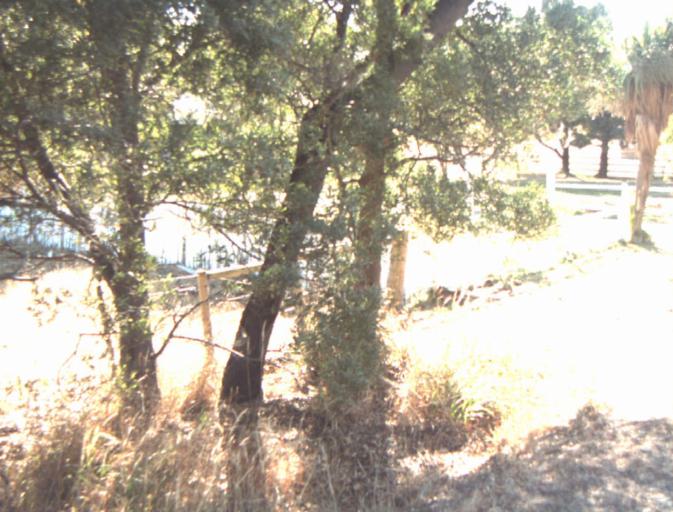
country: AU
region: Tasmania
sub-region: Launceston
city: Newstead
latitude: -41.4465
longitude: 147.2427
